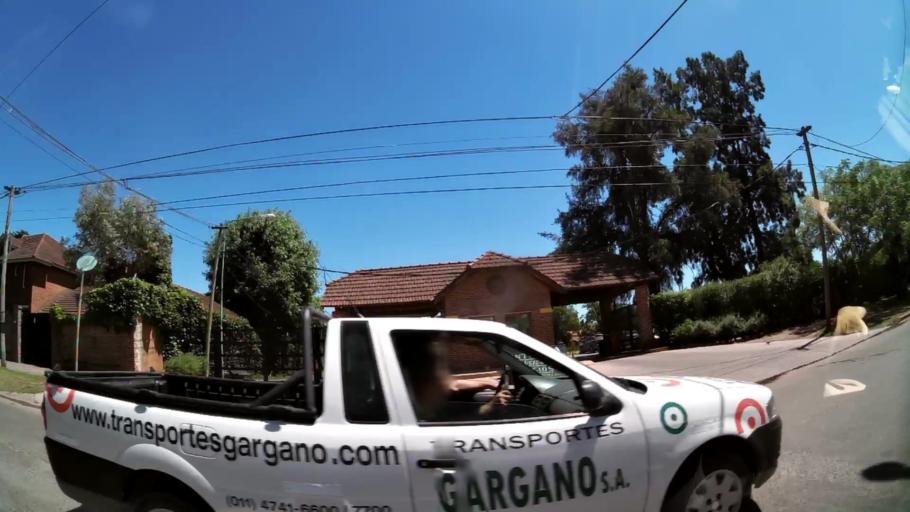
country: AR
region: Buenos Aires
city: Hurlingham
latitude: -34.4976
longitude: -58.6425
